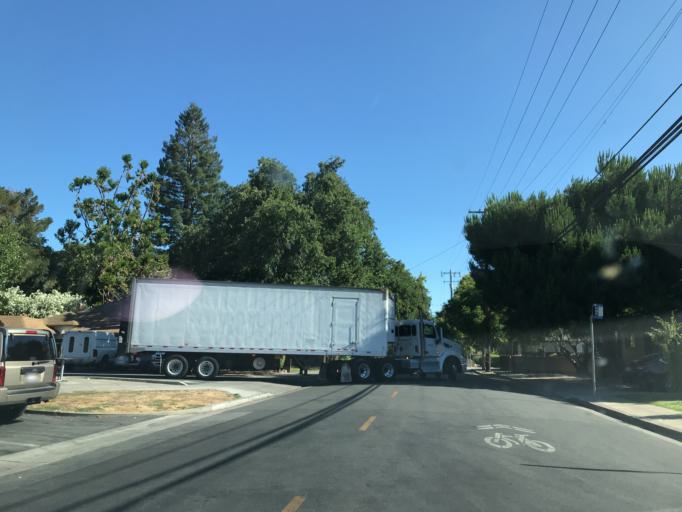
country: US
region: California
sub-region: San Mateo County
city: East Palo Alto
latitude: 37.4593
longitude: -122.1525
